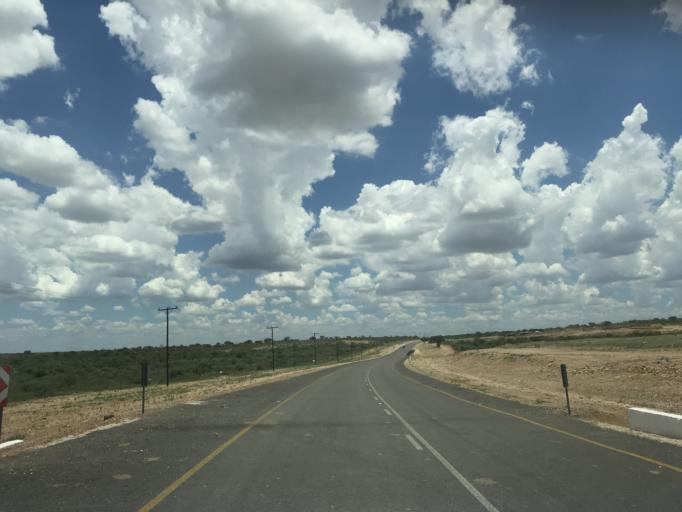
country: BW
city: Mabuli
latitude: -25.7819
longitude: 24.9140
